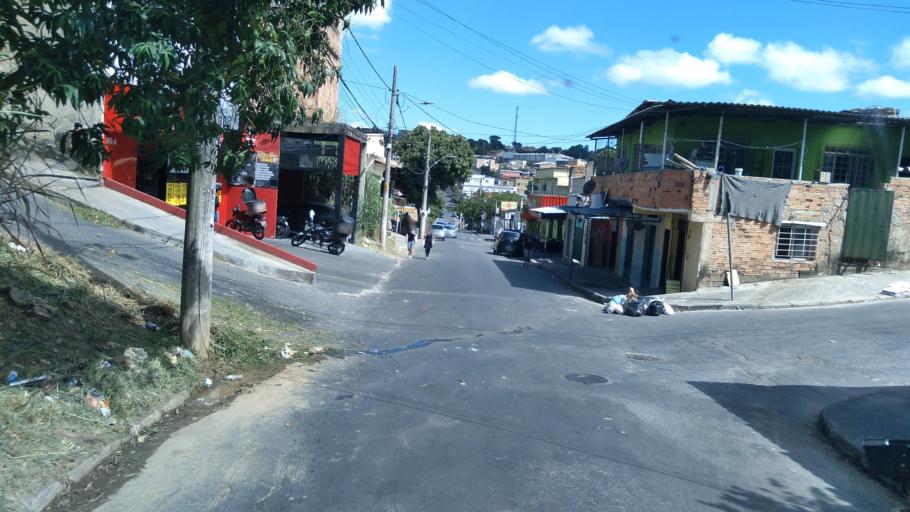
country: BR
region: Minas Gerais
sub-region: Belo Horizonte
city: Belo Horizonte
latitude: -19.8632
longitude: -43.9081
